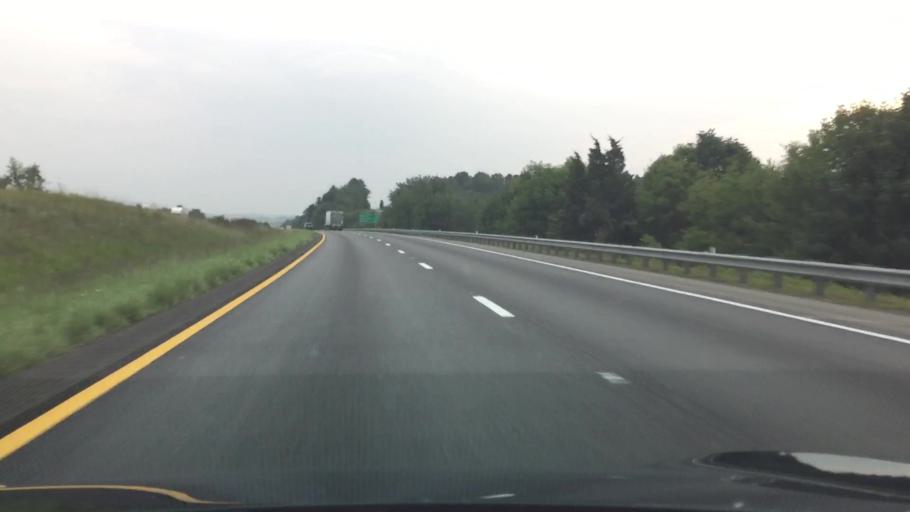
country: US
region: Virginia
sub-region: Montgomery County
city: Christiansburg
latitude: 37.1128
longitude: -80.4384
